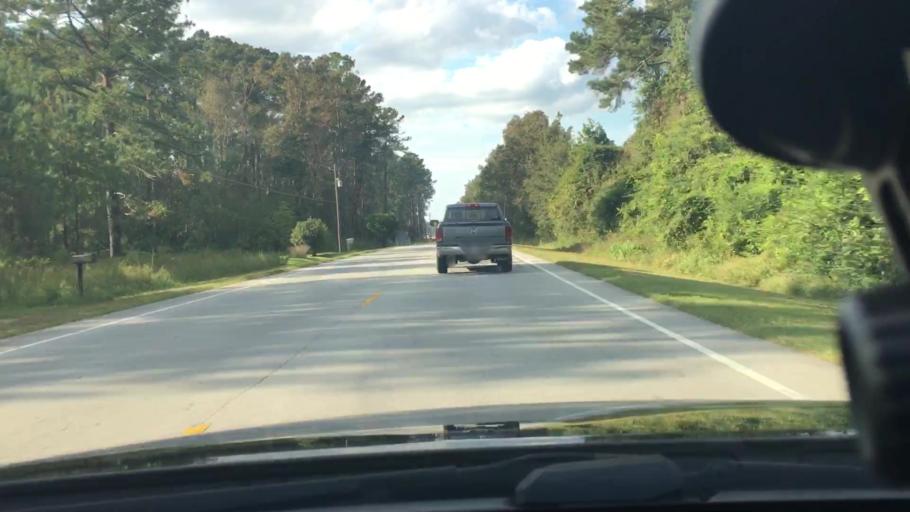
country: US
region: North Carolina
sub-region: Craven County
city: New Bern
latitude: 35.2136
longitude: -77.0627
